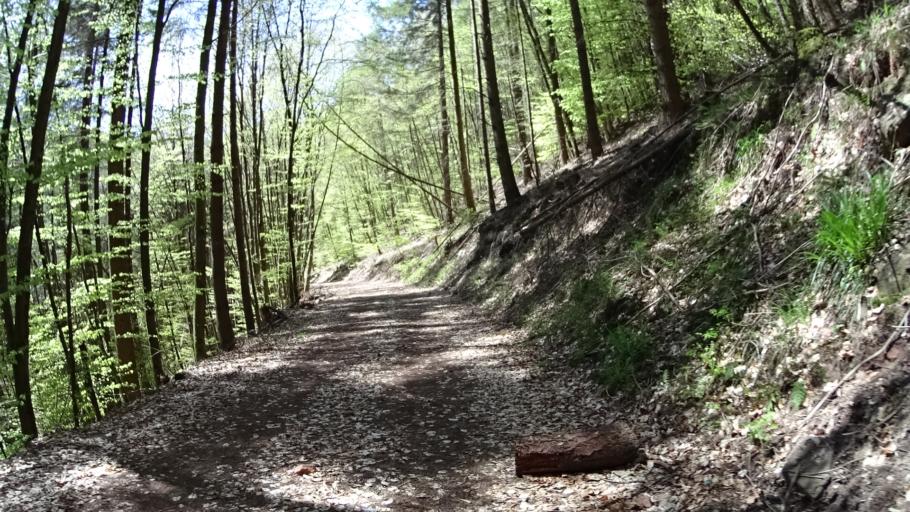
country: DE
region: Rheinland-Pfalz
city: Ramberg
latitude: 49.3063
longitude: 7.9939
